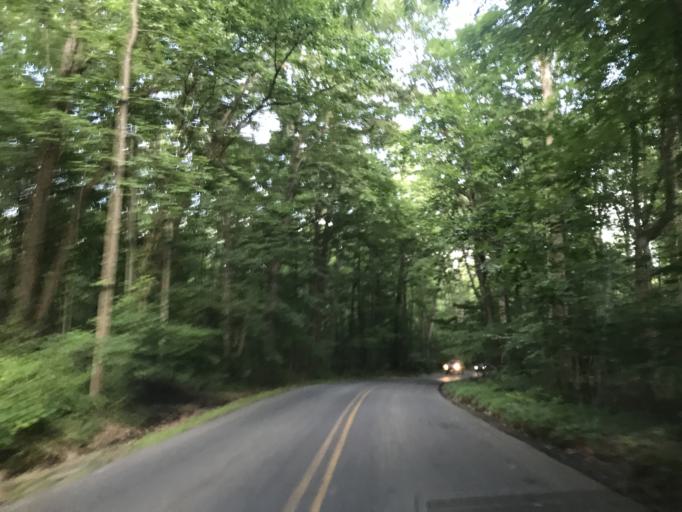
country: US
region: Maryland
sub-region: Harford County
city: Aberdeen
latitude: 39.5226
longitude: -76.2129
